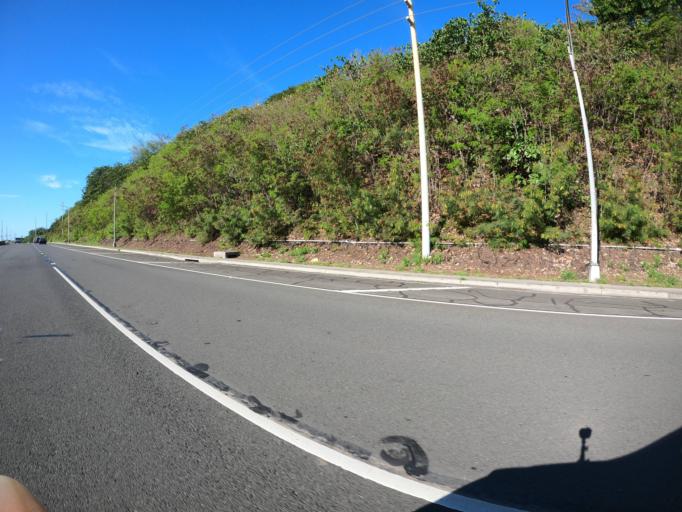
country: US
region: Hawaii
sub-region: Honolulu County
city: Halawa Heights
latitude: 21.3472
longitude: -157.8980
